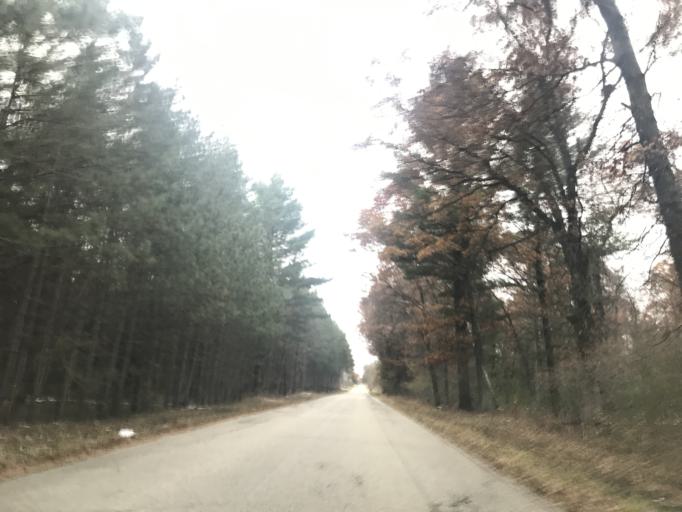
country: US
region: Wisconsin
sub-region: Marinette County
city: Peshtigo
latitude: 45.1156
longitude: -87.7499
